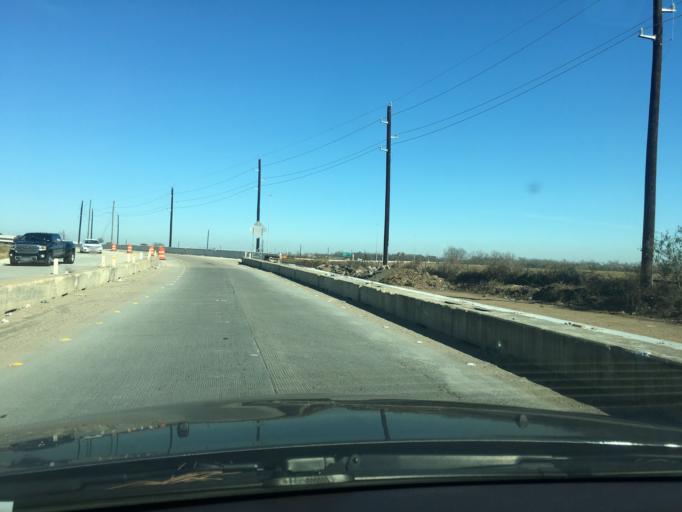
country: US
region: Texas
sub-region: Fort Bend County
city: Richmond
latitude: 29.5454
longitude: -95.7444
